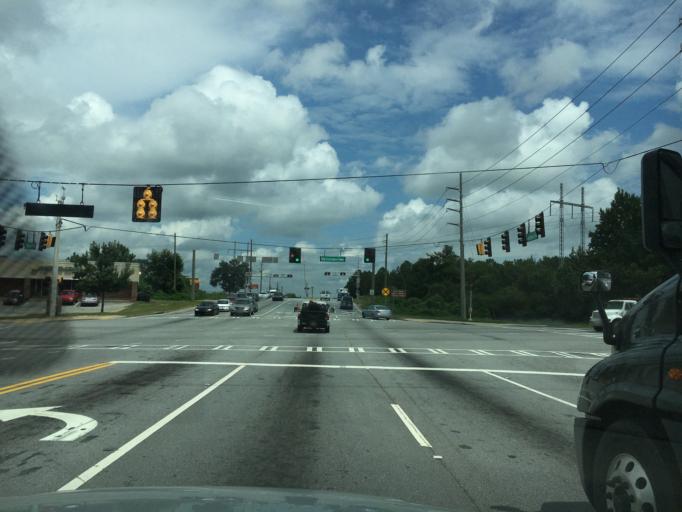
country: US
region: Georgia
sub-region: Rockdale County
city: Lakeview Estates
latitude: 33.6834
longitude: -84.0618
